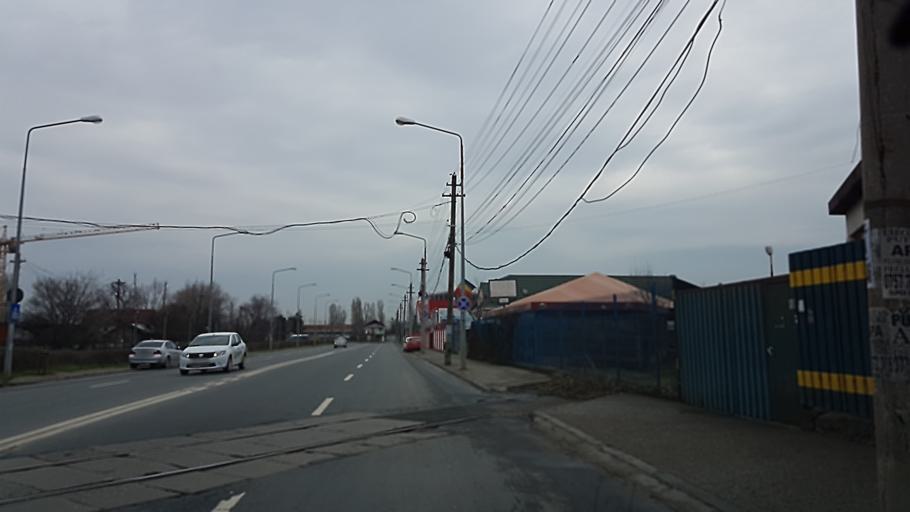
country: RO
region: Ilfov
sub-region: Comuna Glina
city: Catelu
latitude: 44.4276
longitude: 26.2183
